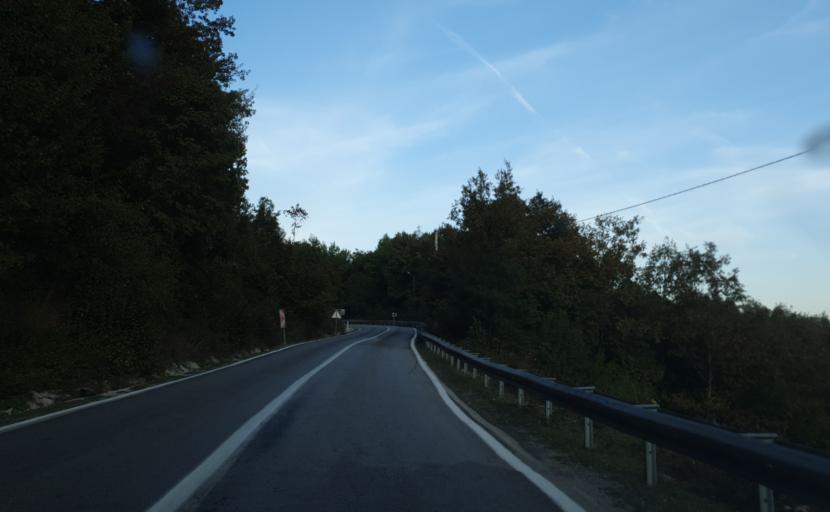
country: TR
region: Kirklareli
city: Sergen
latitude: 41.8222
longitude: 27.7520
